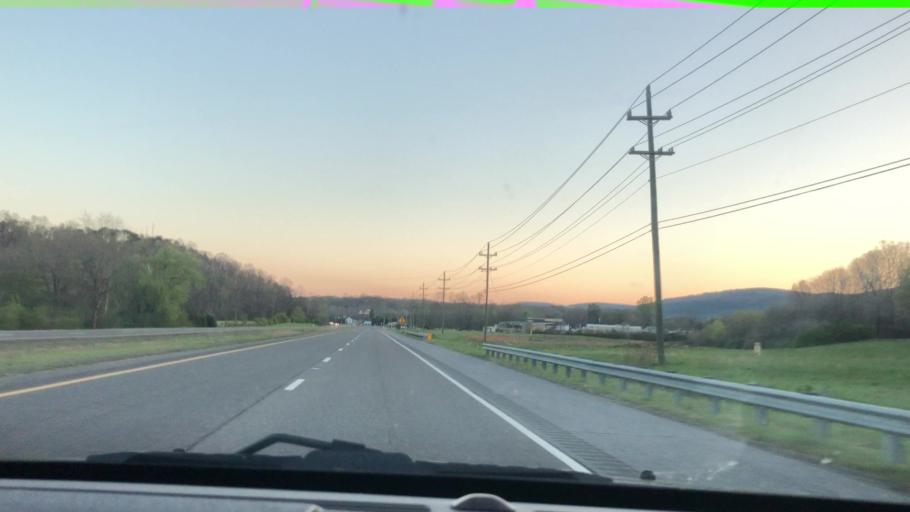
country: US
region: Tennessee
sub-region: Hamilton County
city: Sale Creek
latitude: 35.3489
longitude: -85.1257
